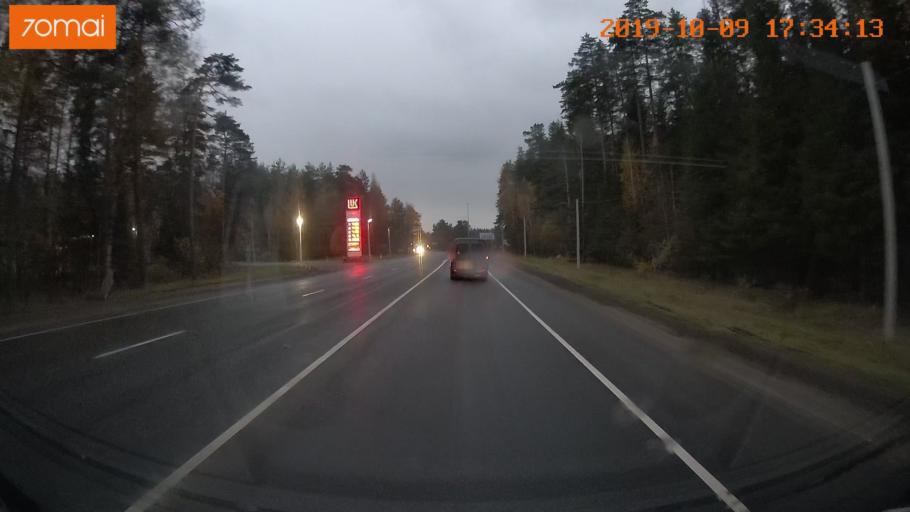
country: RU
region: Ivanovo
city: Bogorodskoye
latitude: 57.1087
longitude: 41.0137
